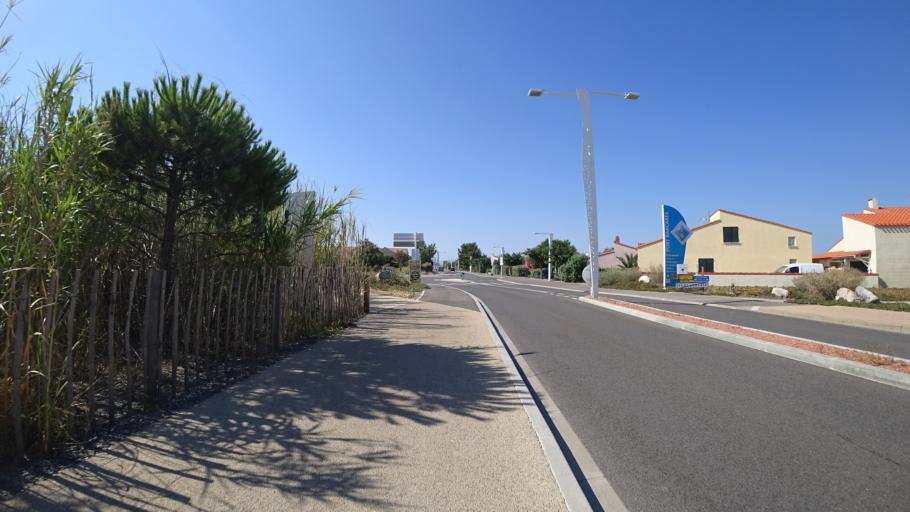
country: FR
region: Languedoc-Roussillon
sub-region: Departement des Pyrenees-Orientales
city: Le Barcares
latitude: 42.8417
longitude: 3.0366
